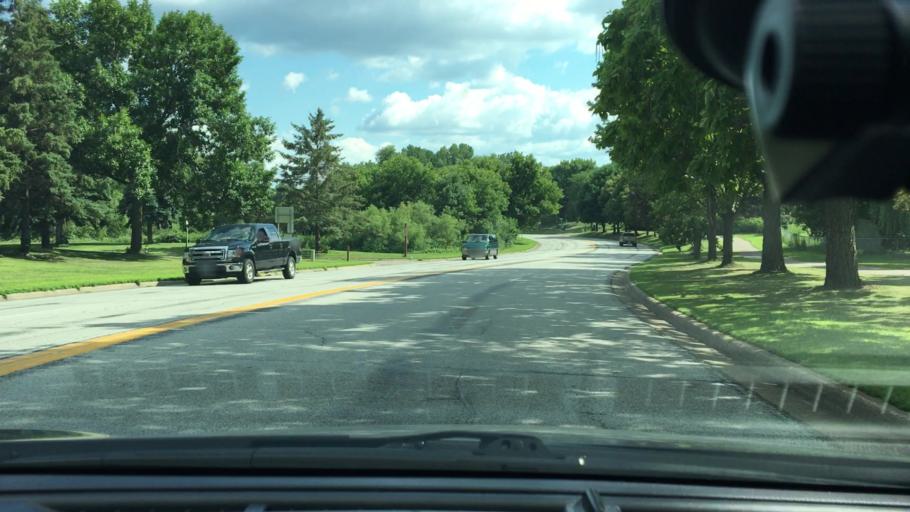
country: US
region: Minnesota
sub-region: Hennepin County
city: New Hope
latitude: 45.0434
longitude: -93.4057
